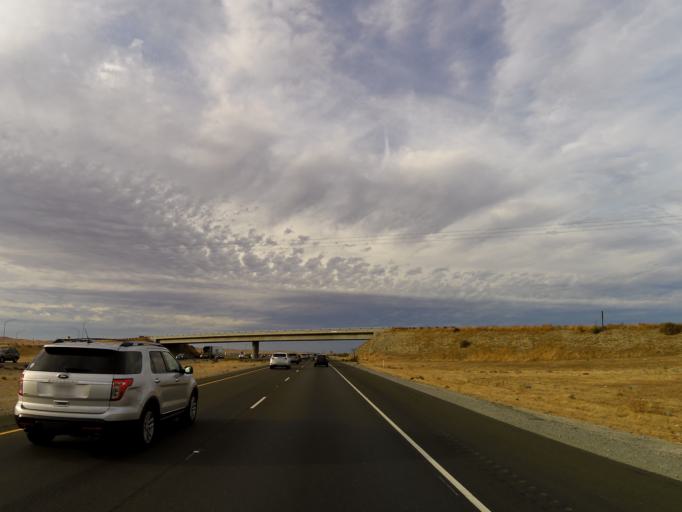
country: US
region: California
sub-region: Kings County
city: Kettleman City
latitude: 35.9334
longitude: -119.9106
